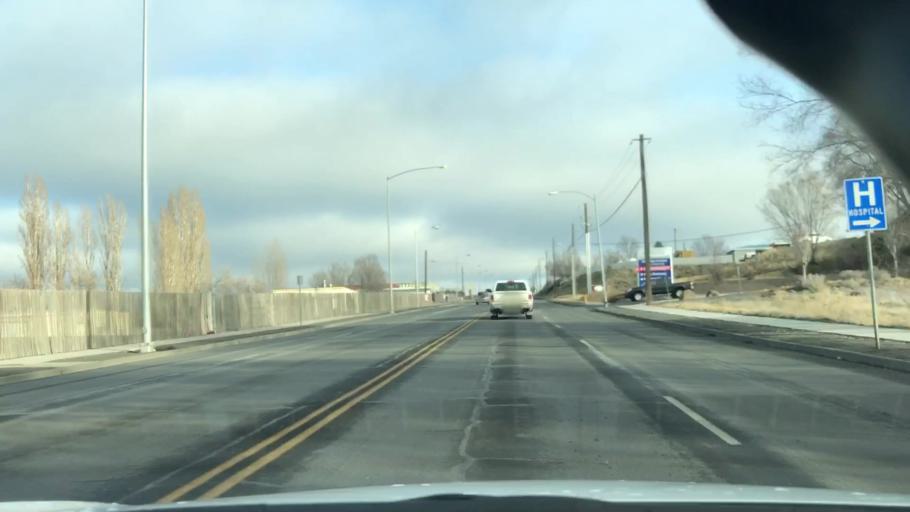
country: US
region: Washington
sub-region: Grant County
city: Moses Lake
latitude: 47.1311
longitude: -119.2655
